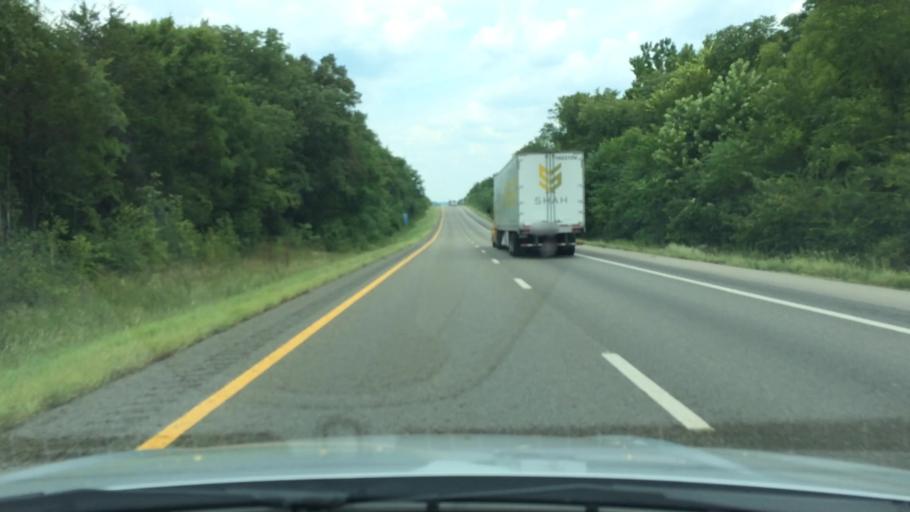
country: US
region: Tennessee
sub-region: Maury County
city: Columbia
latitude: 35.5545
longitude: -86.9074
